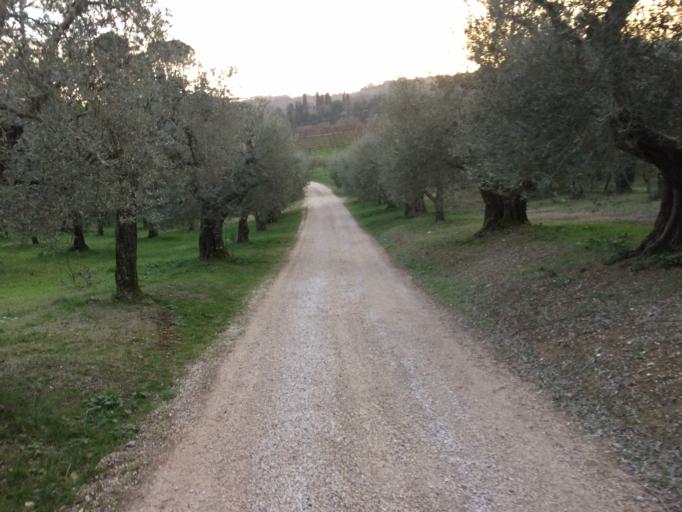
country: IT
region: Umbria
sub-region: Provincia di Perugia
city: Perugia
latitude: 43.0983
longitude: 12.4110
